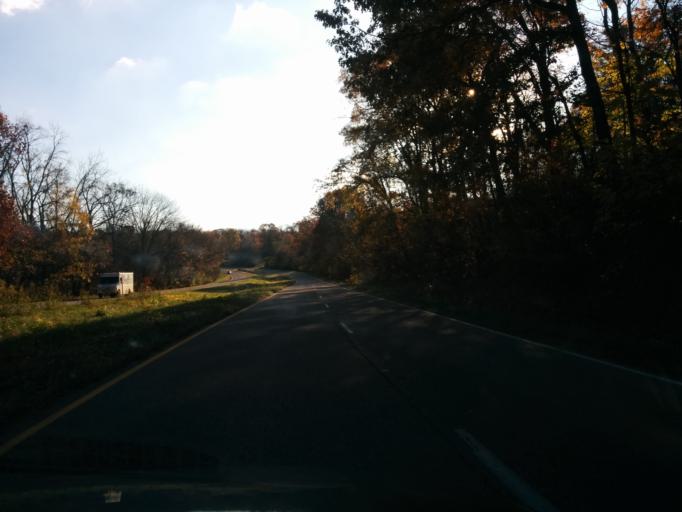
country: US
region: Virginia
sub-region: Rockbridge County
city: East Lexington
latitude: 37.8493
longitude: -79.3452
